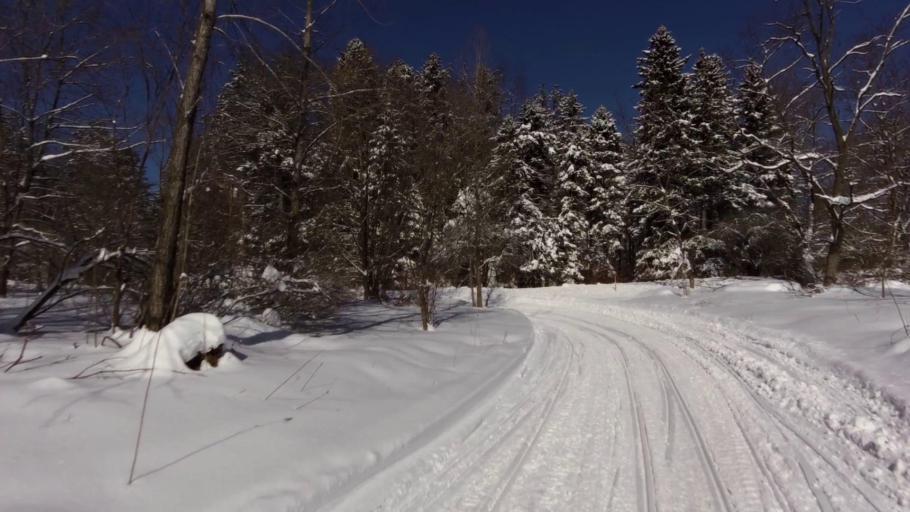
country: US
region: New York
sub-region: Chautauqua County
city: Mayville
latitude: 42.2275
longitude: -79.4077
